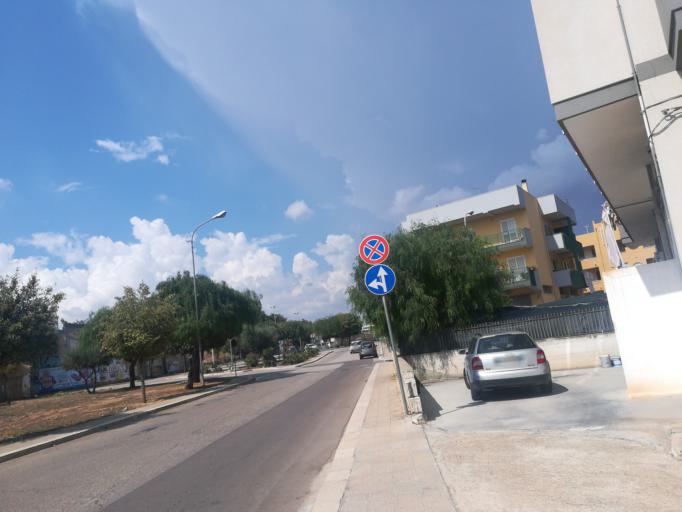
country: IT
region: Apulia
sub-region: Provincia di Bari
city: Polignano a Mare
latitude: 40.9885
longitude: 17.2286
